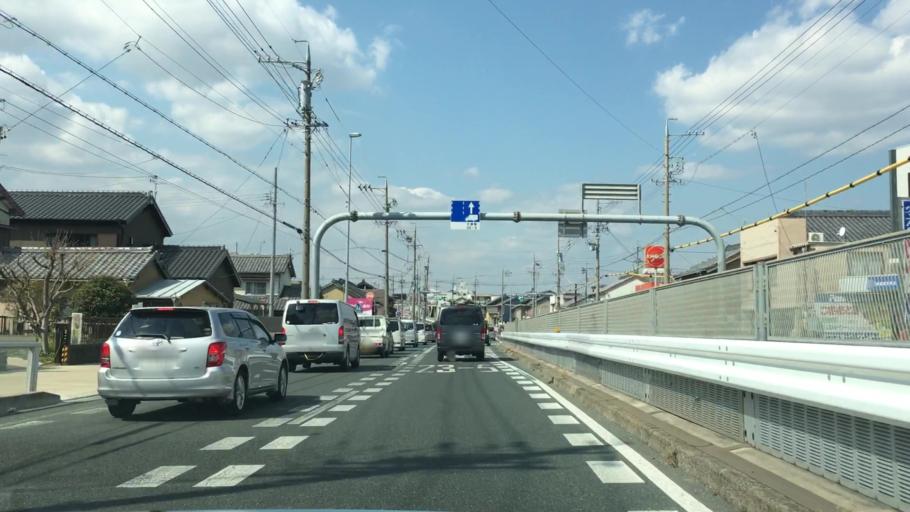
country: JP
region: Aichi
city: Toyohashi
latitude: 34.7570
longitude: 137.4094
